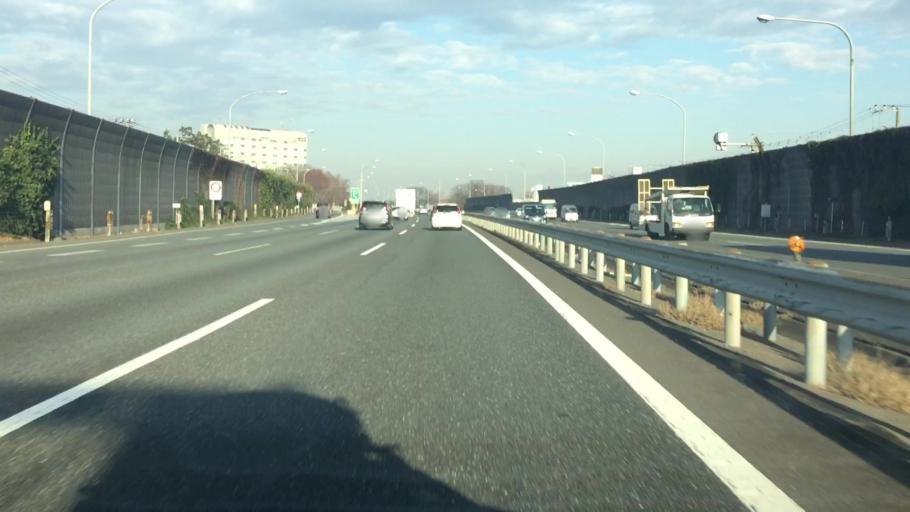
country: JP
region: Saitama
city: Sakado
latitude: 35.9433
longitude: 139.4012
